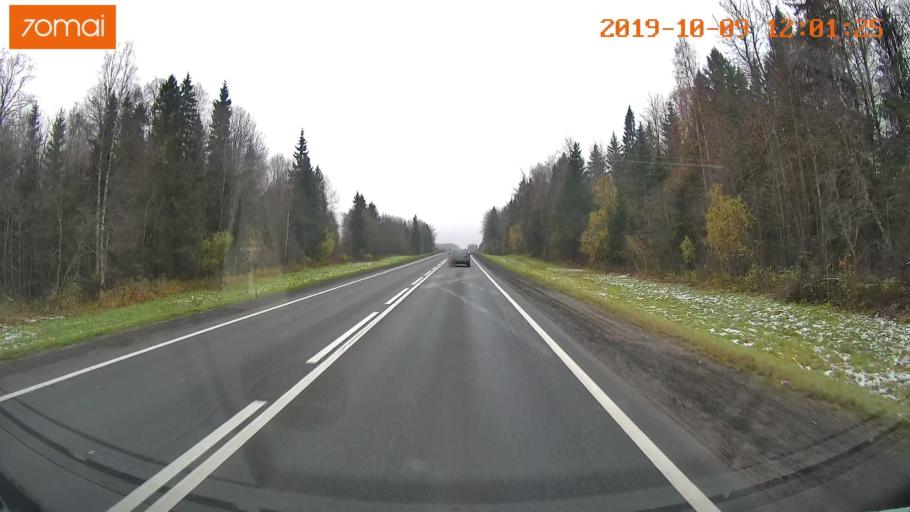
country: RU
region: Vologda
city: Gryazovets
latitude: 58.6882
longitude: 40.3034
